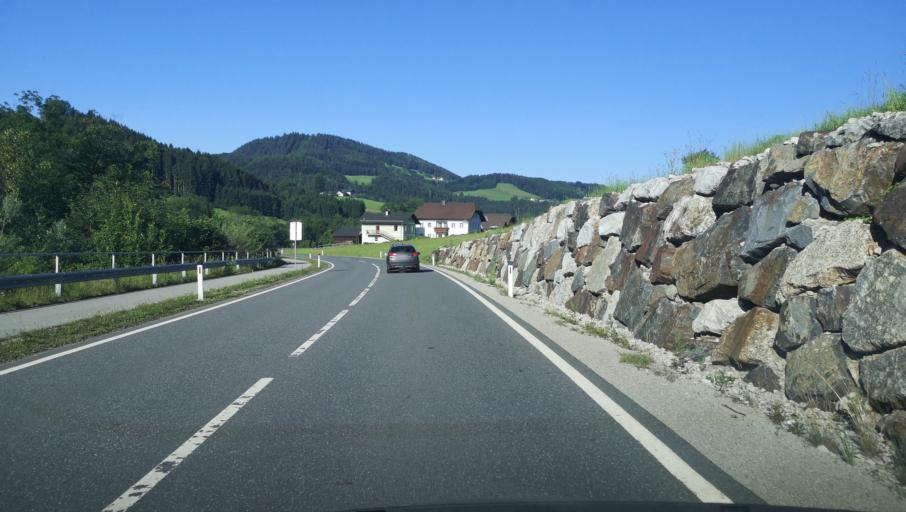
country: AT
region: Lower Austria
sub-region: Politischer Bezirk Amstetten
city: Ybbsitz
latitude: 47.9437
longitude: 14.8696
